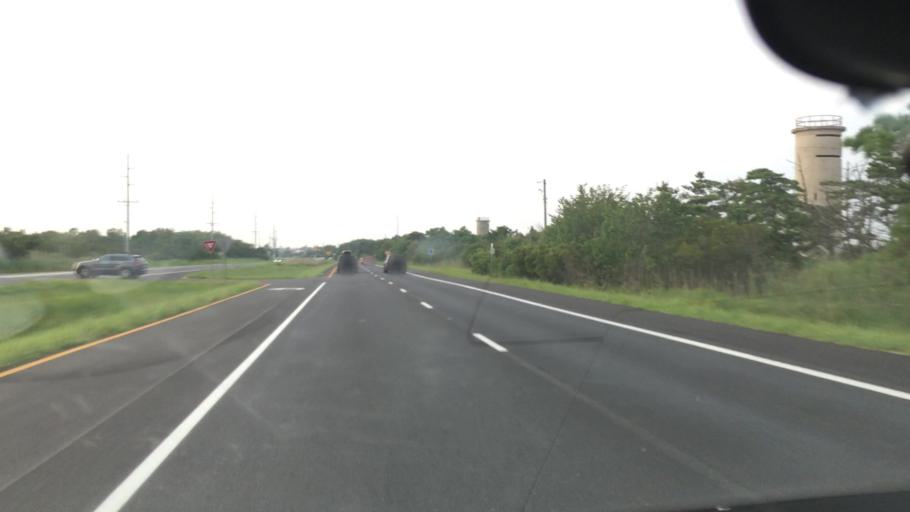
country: US
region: Delaware
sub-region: Sussex County
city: Rehoboth Beach
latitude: 38.6773
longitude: -75.0717
